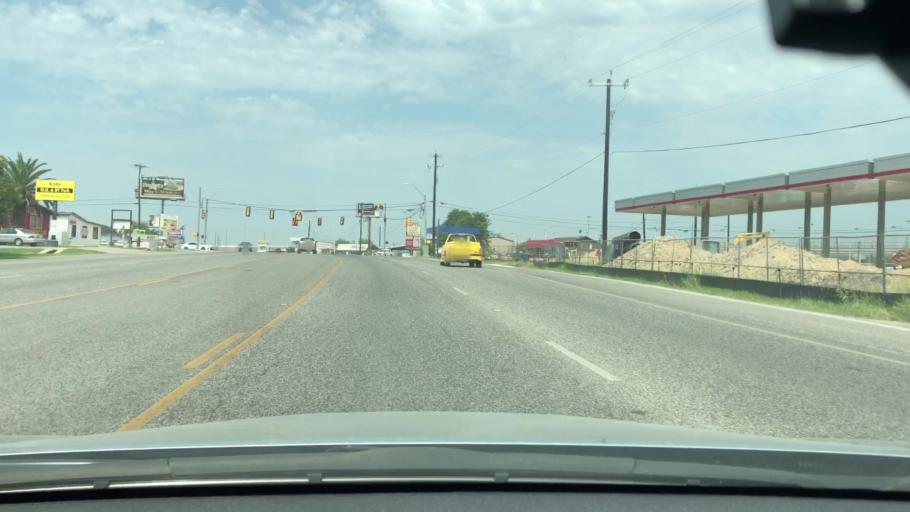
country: US
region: Texas
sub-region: Bexar County
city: Kirby
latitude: 29.4749
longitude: -98.3799
